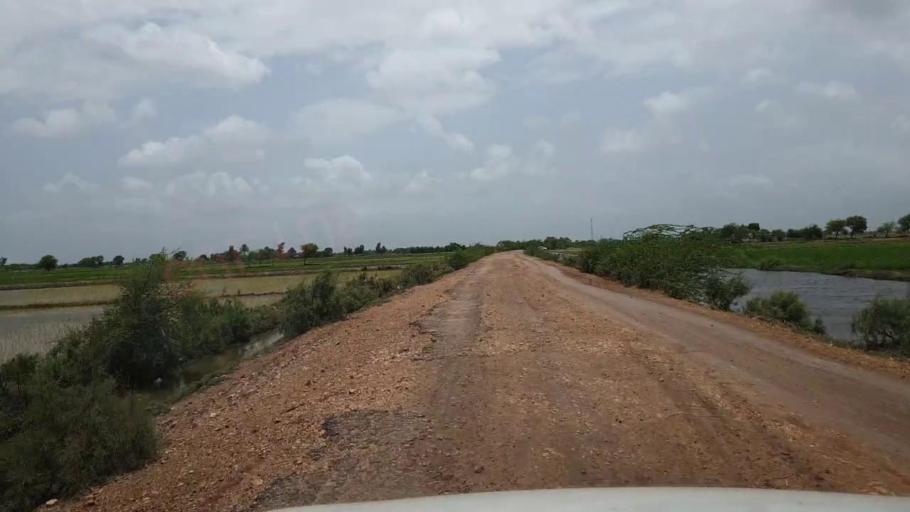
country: PK
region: Sindh
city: Kario
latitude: 24.7202
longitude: 68.5718
